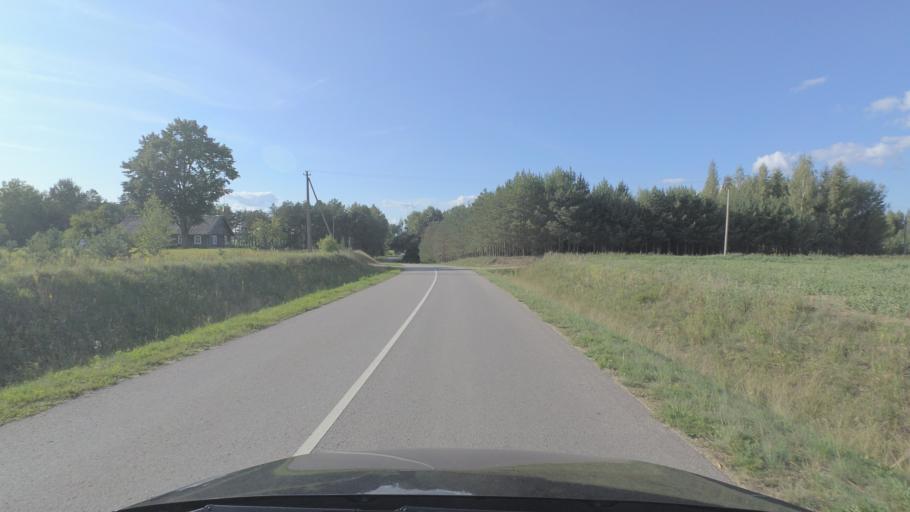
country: LT
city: Pabrade
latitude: 55.0929
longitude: 25.6847
